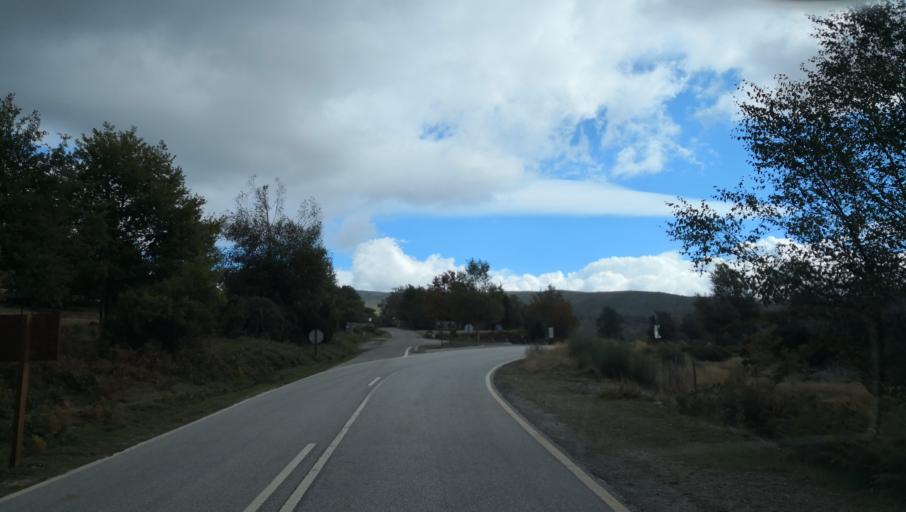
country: PT
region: Vila Real
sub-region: Vila Real
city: Vila Real
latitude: 41.3717
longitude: -7.8027
